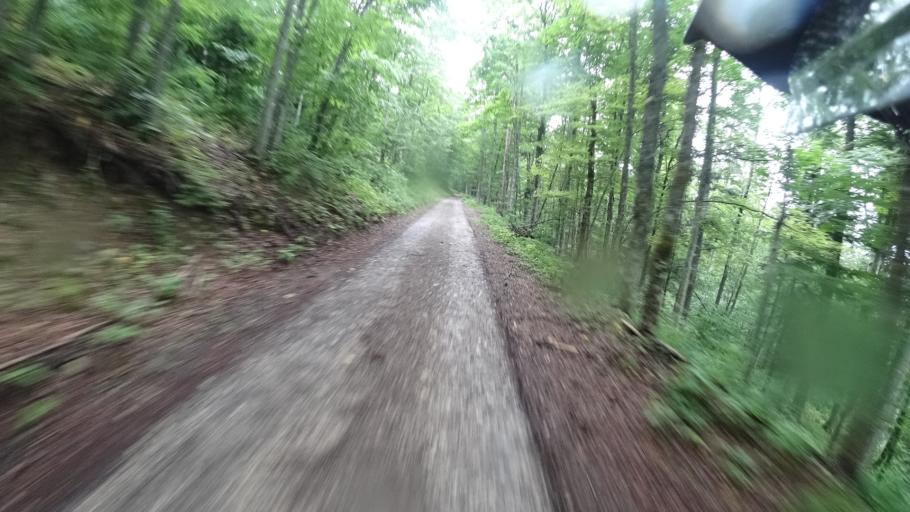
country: HR
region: Primorsko-Goranska
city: Vrbovsko
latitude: 45.3013
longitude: 14.9320
